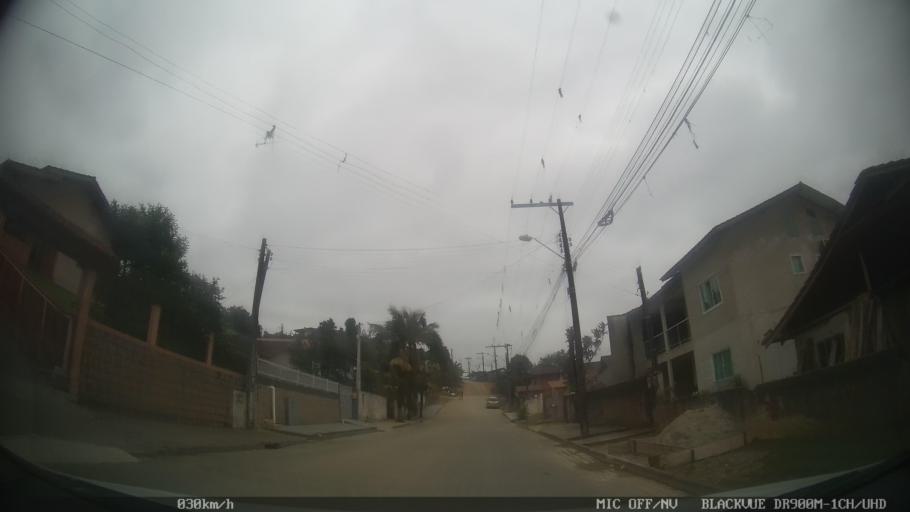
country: BR
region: Santa Catarina
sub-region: Joinville
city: Joinville
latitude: -26.3493
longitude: -48.8265
